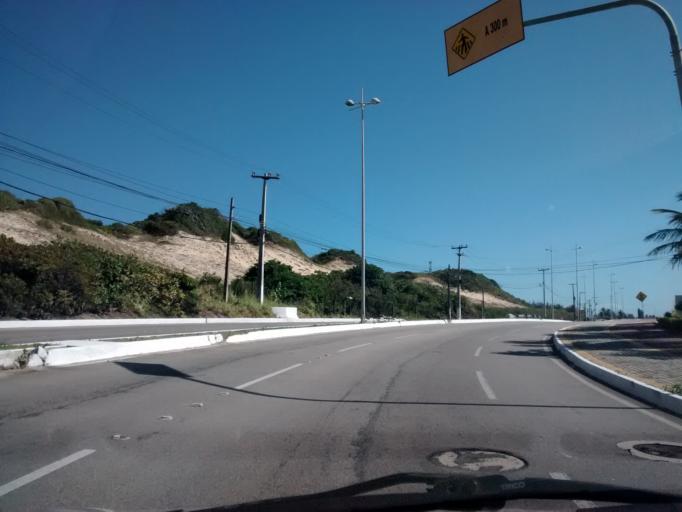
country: BR
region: Rio Grande do Norte
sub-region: Natal
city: Natal
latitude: -5.8040
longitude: -35.1826
